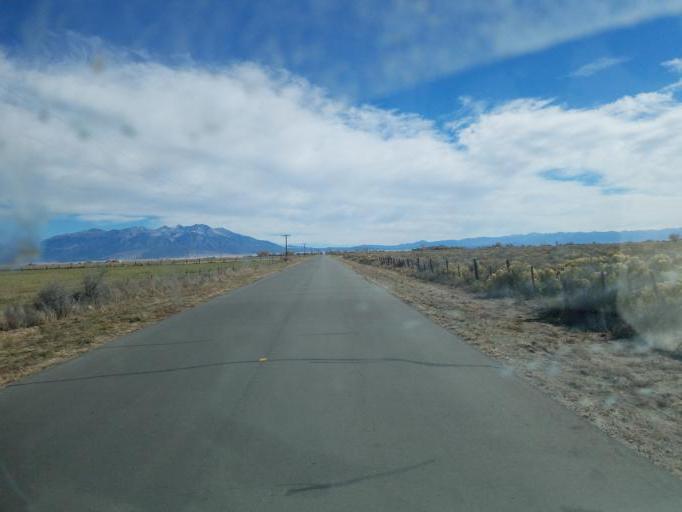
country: US
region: Colorado
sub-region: Alamosa County
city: Alamosa East
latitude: 37.5025
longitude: -105.8327
